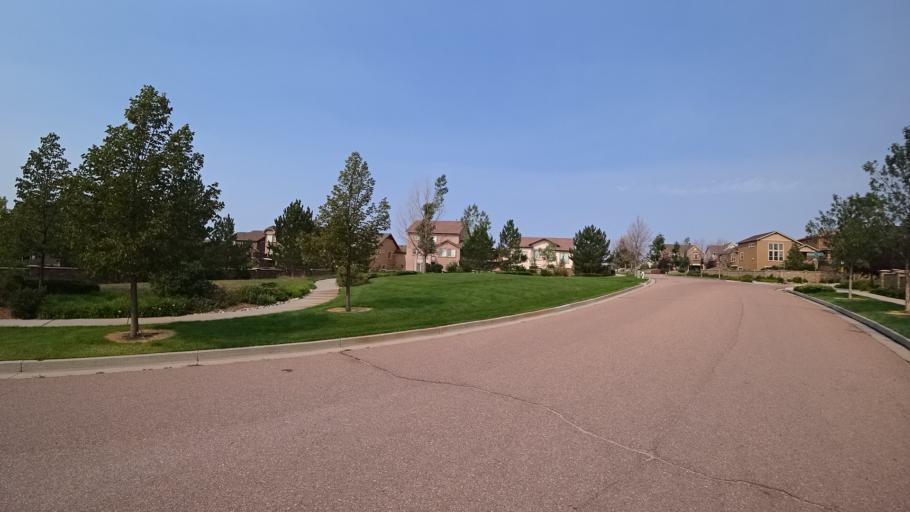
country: US
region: Colorado
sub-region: El Paso County
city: Black Forest
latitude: 38.9690
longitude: -104.7317
